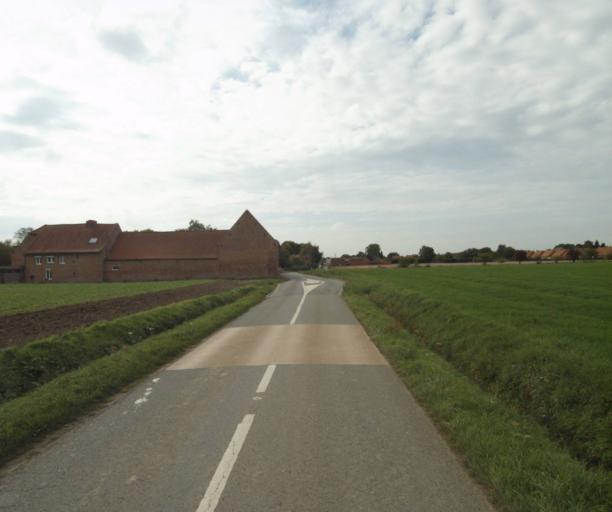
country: FR
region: Nord-Pas-de-Calais
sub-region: Departement du Nord
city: Marquillies
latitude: 50.5565
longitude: 2.8777
